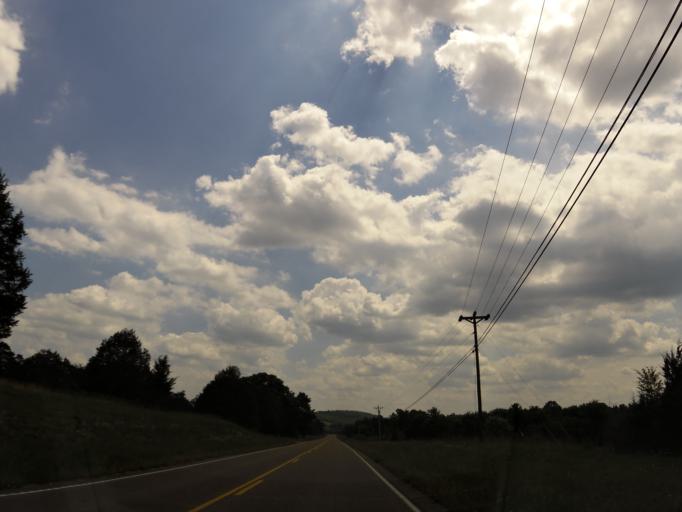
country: US
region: Tennessee
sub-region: Bledsoe County
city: Pikeville
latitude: 35.5523
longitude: -85.2532
